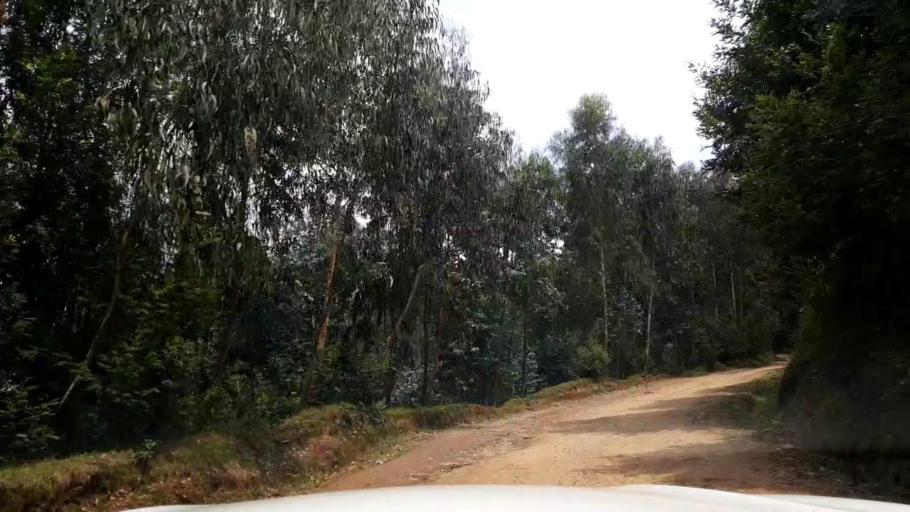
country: RW
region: Western Province
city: Kibuye
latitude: -1.9361
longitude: 29.4486
